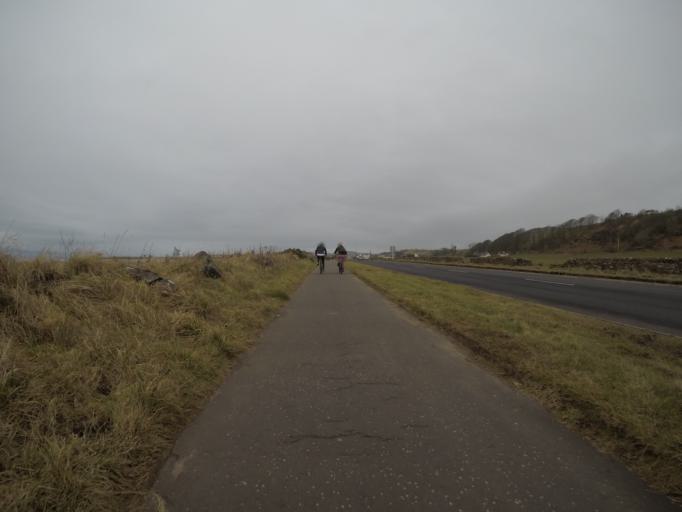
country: GB
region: Scotland
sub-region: North Ayrshire
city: West Kilbride
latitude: 55.6730
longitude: -4.8495
